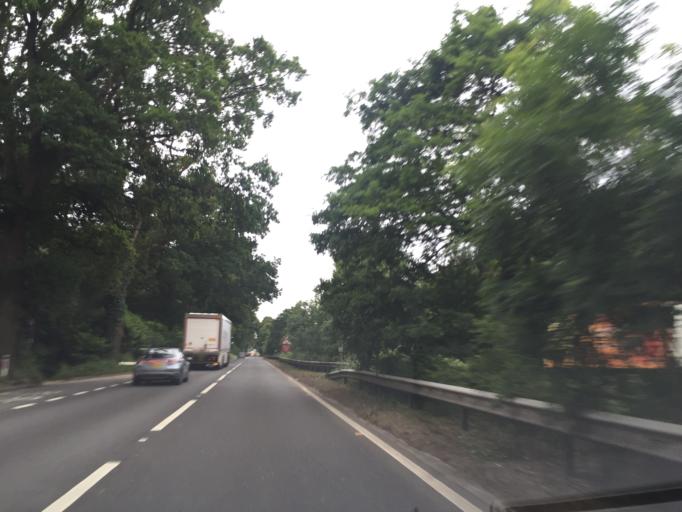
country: GB
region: England
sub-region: Dorset
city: St Leonards
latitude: 50.8245
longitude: -1.8469
